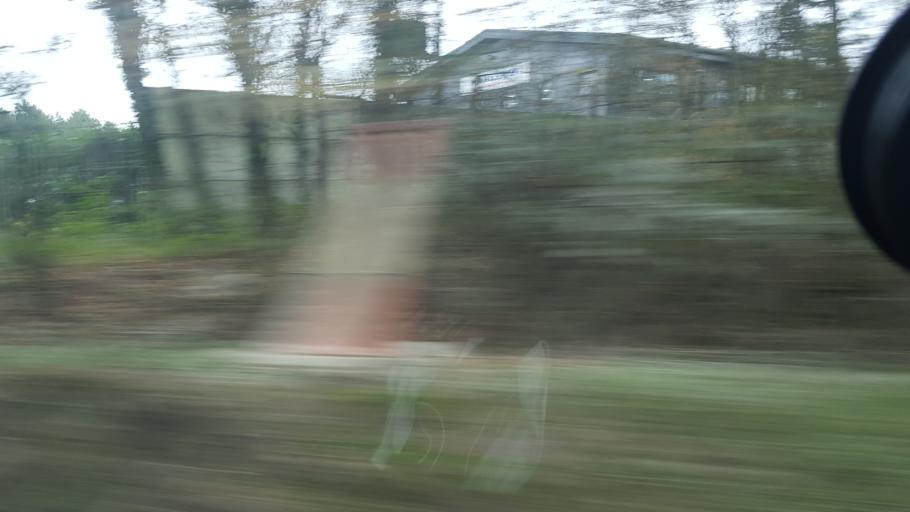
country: GB
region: England
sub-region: Hampshire
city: Eversley
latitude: 51.3255
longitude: -0.8711
